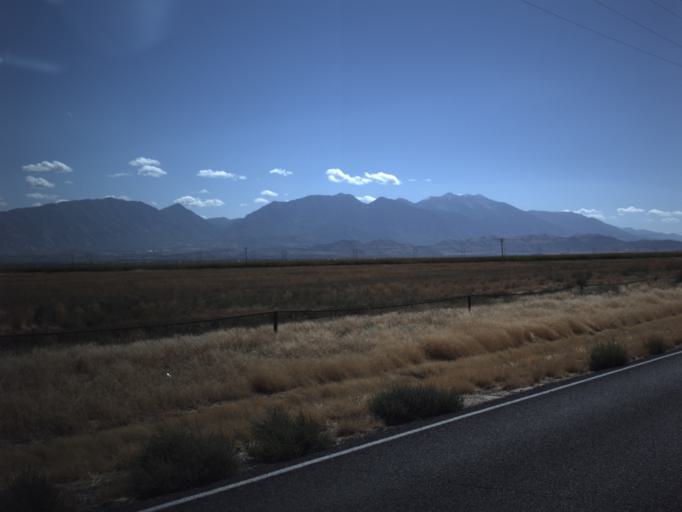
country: US
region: Utah
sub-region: Utah County
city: Genola
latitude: 40.0788
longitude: -111.9587
